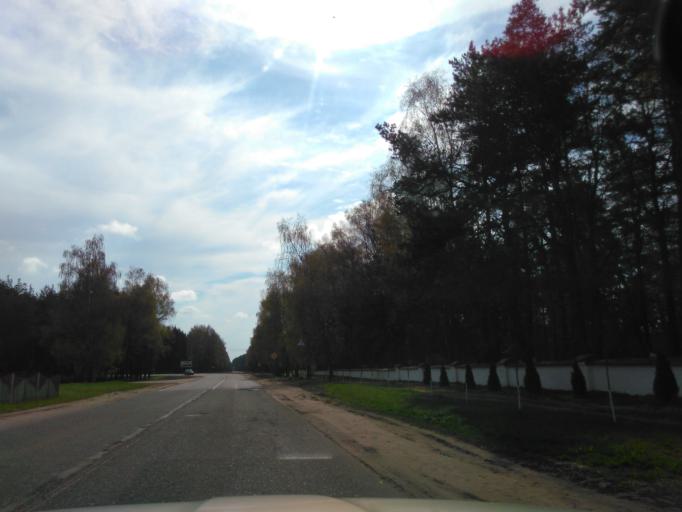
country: BY
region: Minsk
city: Rakaw
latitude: 53.9664
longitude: 27.0695
